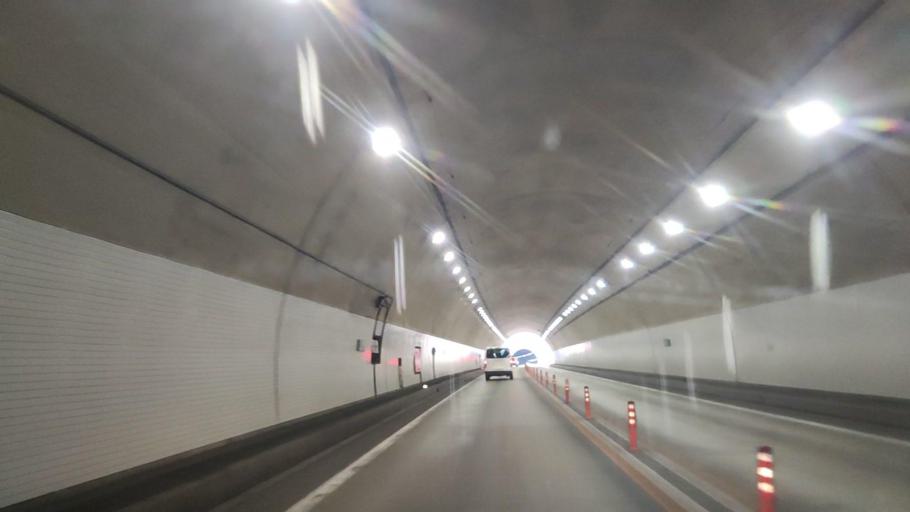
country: JP
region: Akita
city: Odate
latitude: 40.3398
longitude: 140.6241
